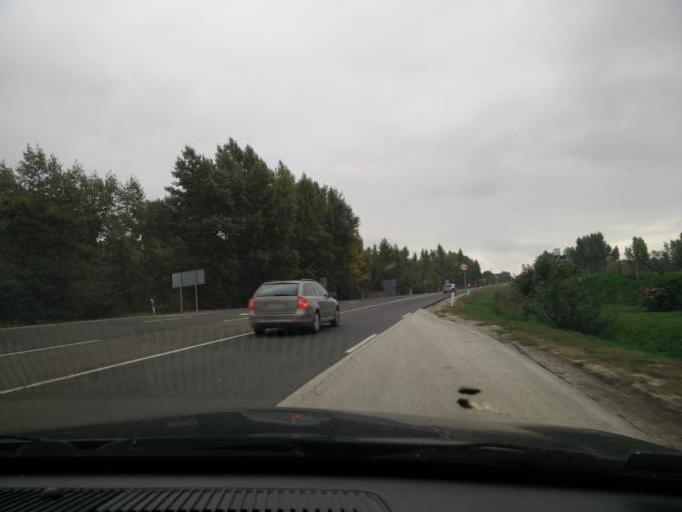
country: HU
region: Komarom-Esztergom
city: Dorog
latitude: 47.7471
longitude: 18.7365
